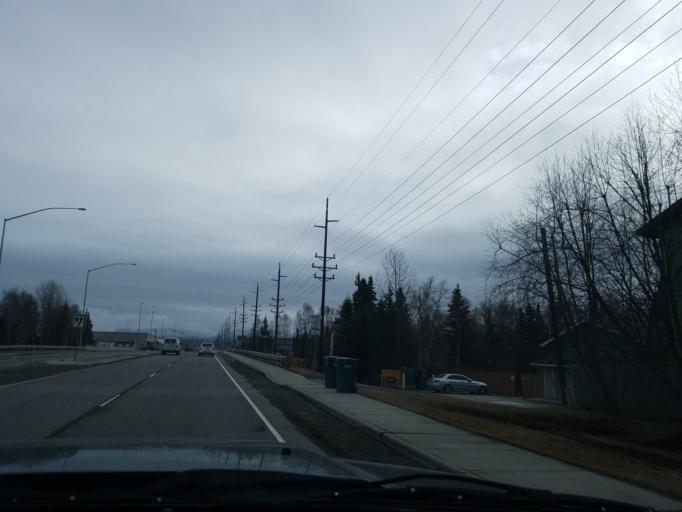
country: US
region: Alaska
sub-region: Anchorage Municipality
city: Anchorage
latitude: 61.1664
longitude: -149.8763
